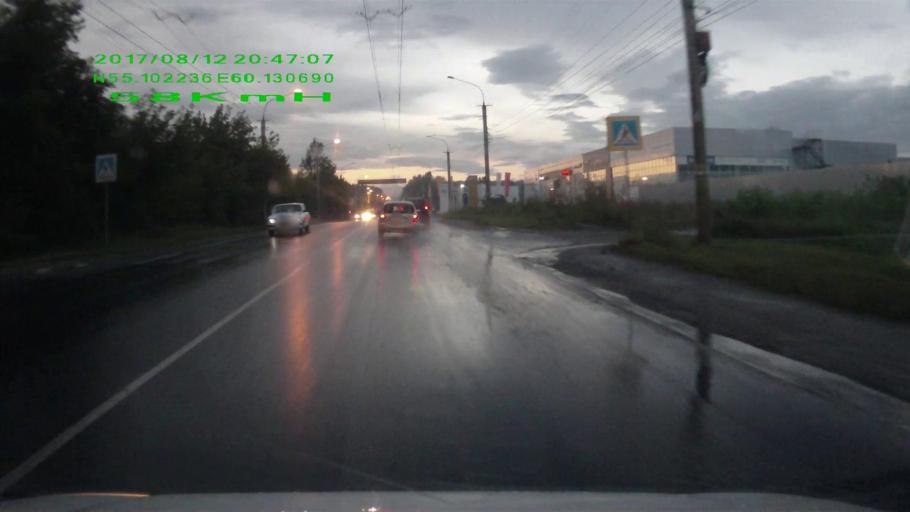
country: RU
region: Chelyabinsk
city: Turgoyak
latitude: 55.1026
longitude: 60.1307
